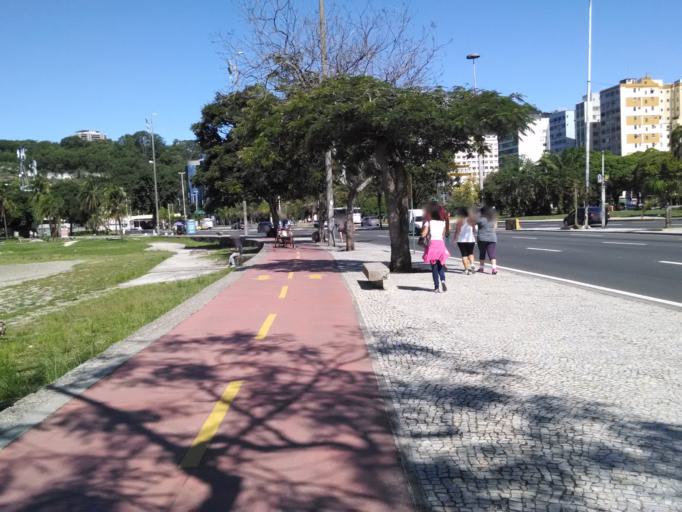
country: BR
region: Rio de Janeiro
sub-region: Rio De Janeiro
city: Rio de Janeiro
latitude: -22.9471
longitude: -43.1815
